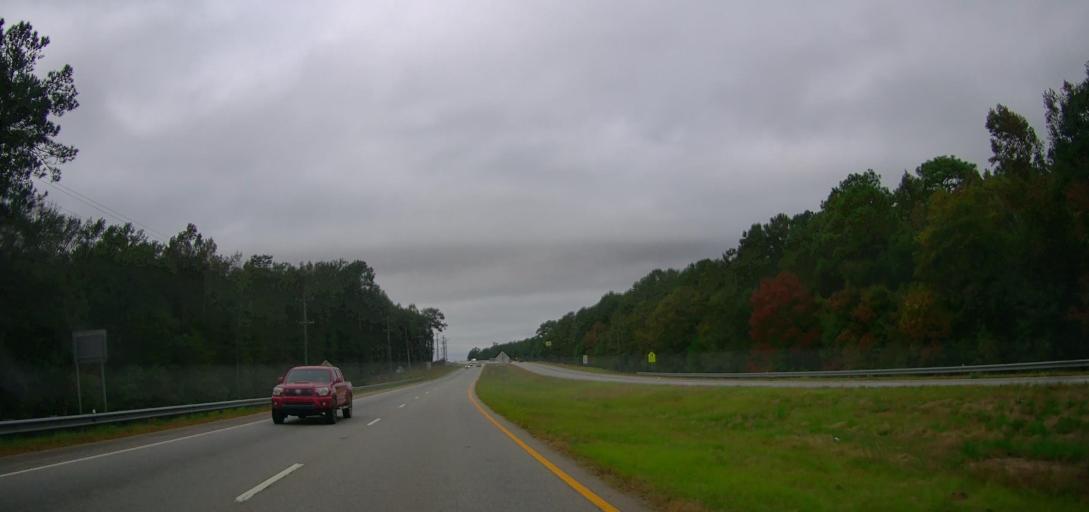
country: US
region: Georgia
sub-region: Thomas County
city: Thomasville
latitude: 30.8741
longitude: -83.9585
